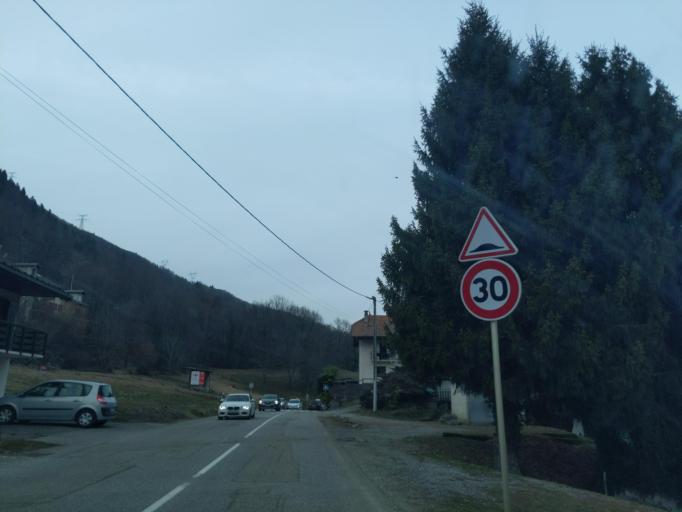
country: FR
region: Rhone-Alpes
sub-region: Departement de la Savoie
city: La Bathie
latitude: 45.6196
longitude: 6.4333
